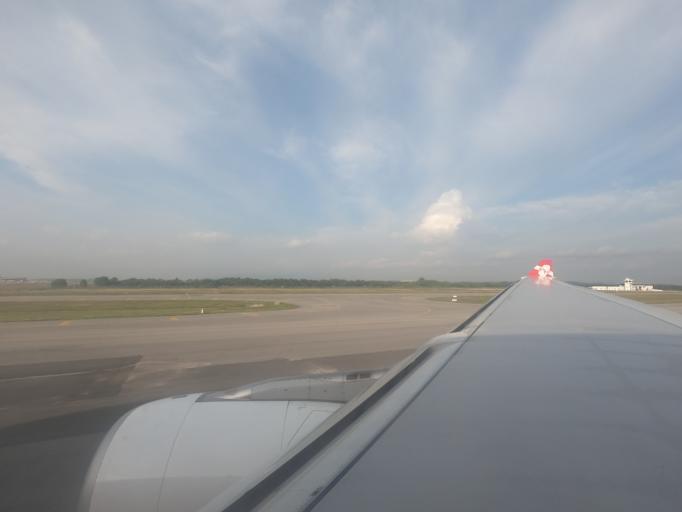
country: MY
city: Sungai Pelek New Village
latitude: 2.7277
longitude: 101.6861
